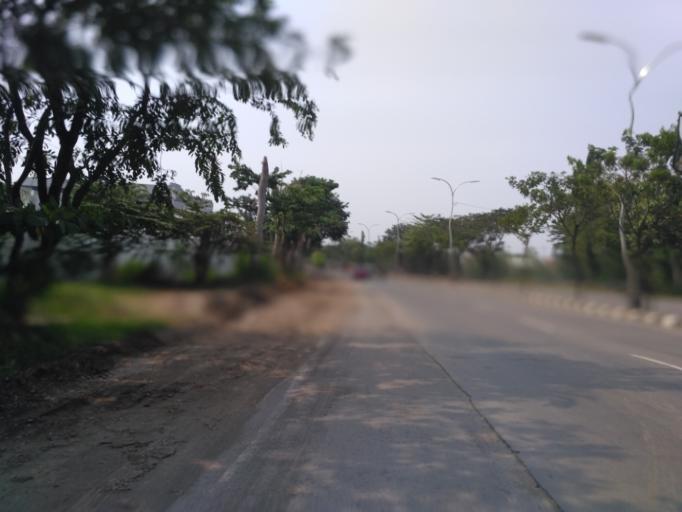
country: ID
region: Central Java
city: Semarang
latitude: -6.9697
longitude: 110.3917
